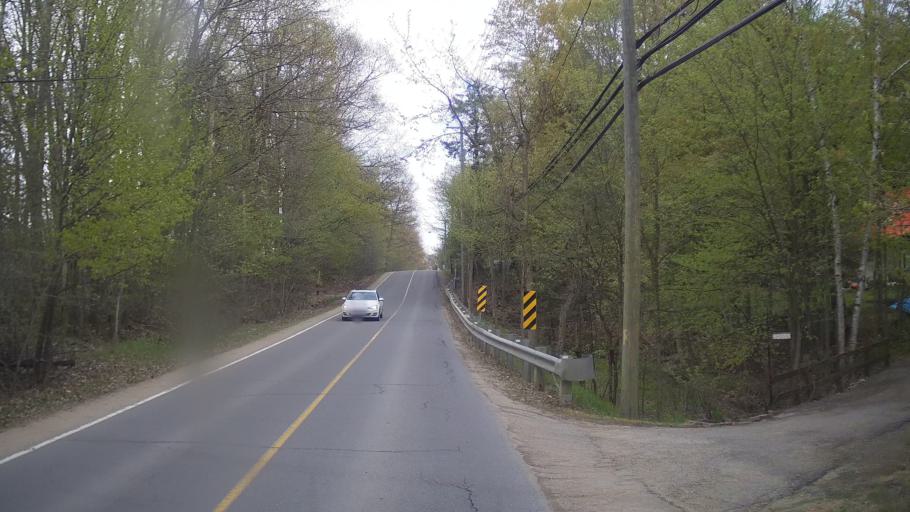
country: CA
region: Quebec
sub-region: Monteregie
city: Hudson
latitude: 45.4544
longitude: -74.1604
